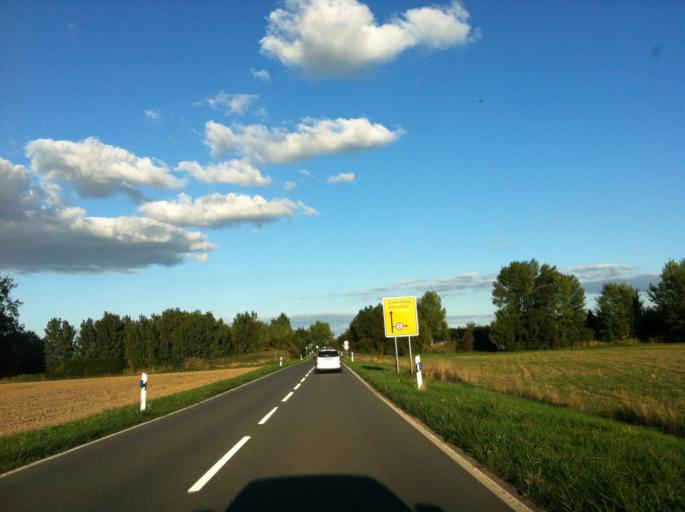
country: DE
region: Rheinland-Pfalz
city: Oppenheim
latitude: 49.8679
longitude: 8.3651
